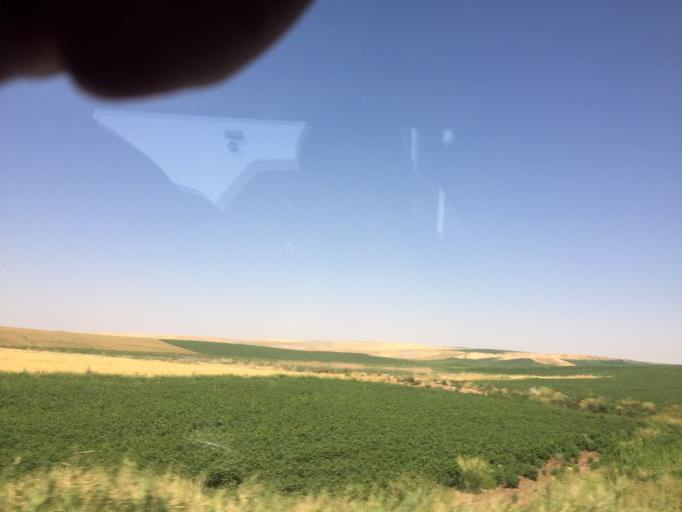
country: TR
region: Diyarbakir
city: Salat
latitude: 37.8573
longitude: 40.8620
